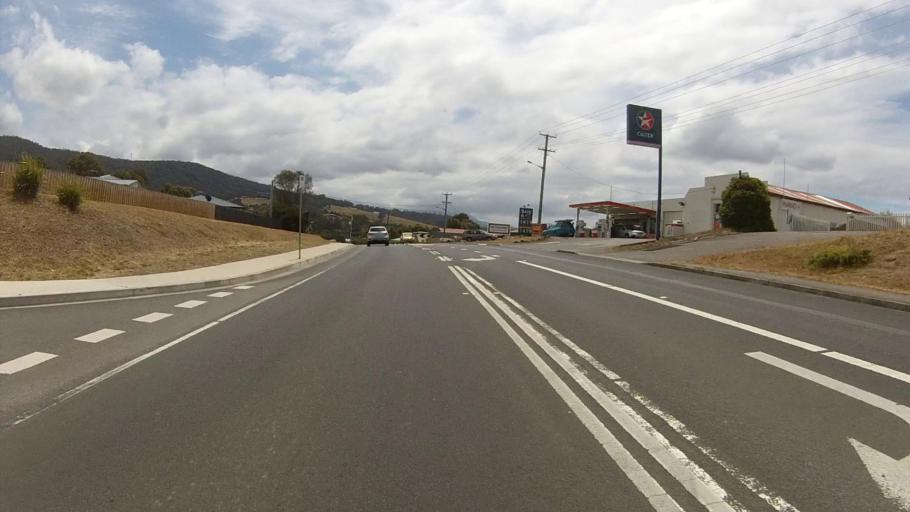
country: AU
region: Tasmania
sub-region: Kingborough
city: Margate
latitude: -43.0694
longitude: 147.2567
